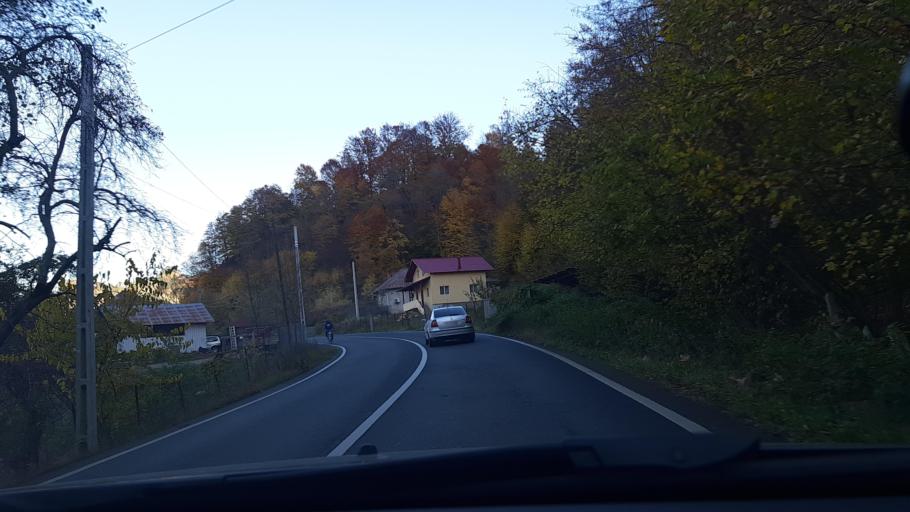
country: RO
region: Valcea
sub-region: Comuna Brezoi
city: Brezoi
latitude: 45.3435
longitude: 24.2262
